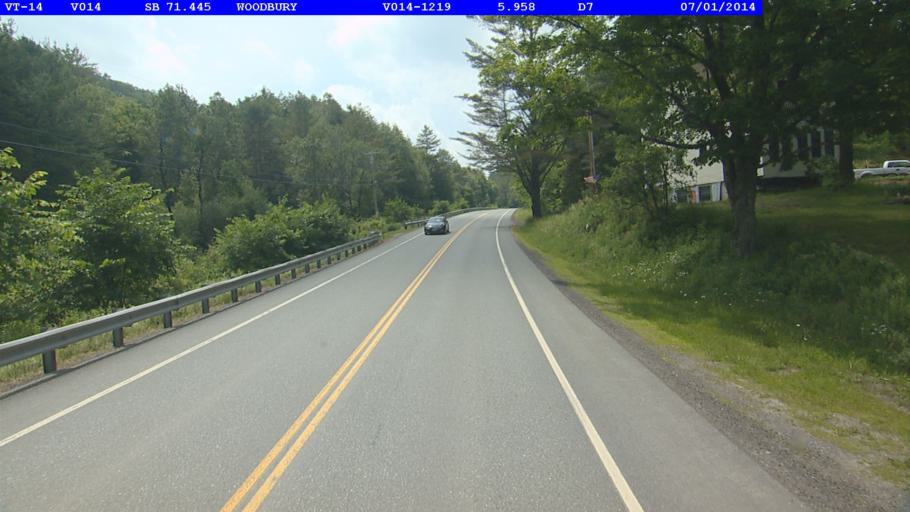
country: US
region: Vermont
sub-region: Caledonia County
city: Hardwick
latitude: 44.4689
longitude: -72.4059
